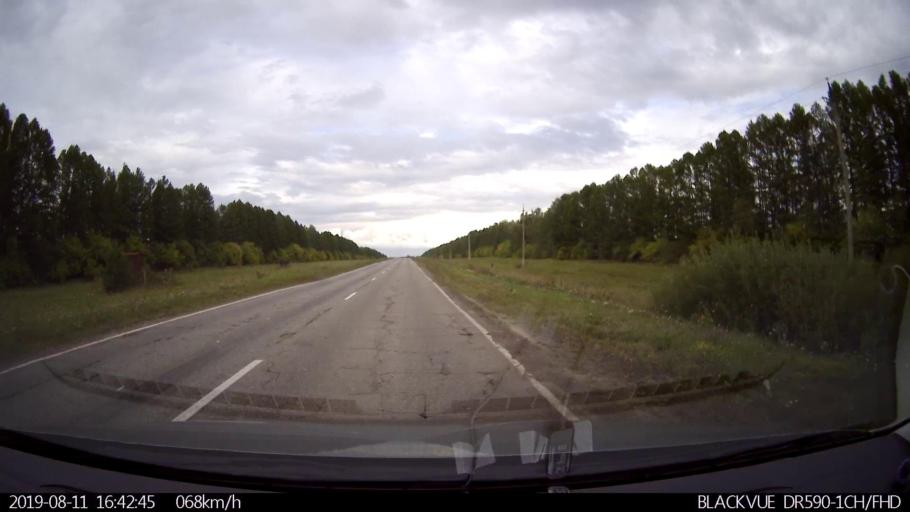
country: RU
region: Ulyanovsk
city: Mayna
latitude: 54.1631
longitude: 47.6653
